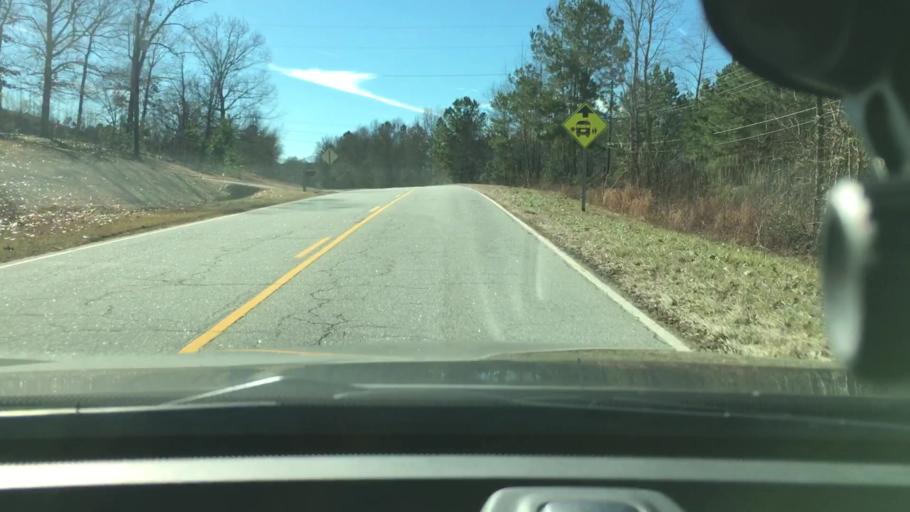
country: US
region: South Carolina
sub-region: Cherokee County
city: Gaffney
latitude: 35.0461
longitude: -81.6748
